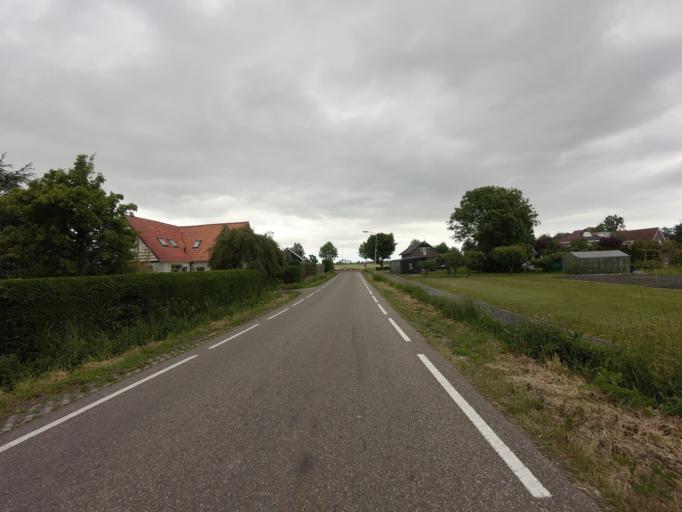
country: NL
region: North Holland
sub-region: Gemeente Hoorn
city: Hoorn
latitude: 52.6407
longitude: 5.0106
